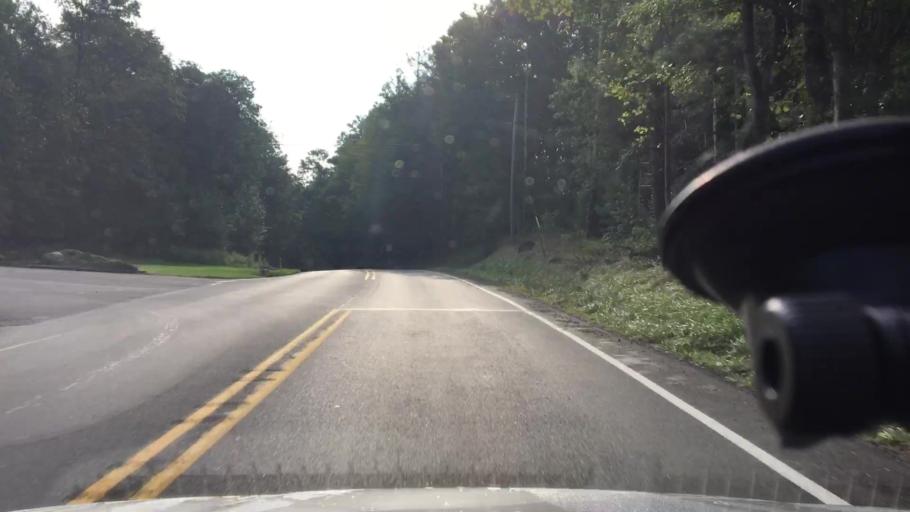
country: US
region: Pennsylvania
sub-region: Monroe County
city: Parkside
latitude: 41.1256
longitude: -75.2927
